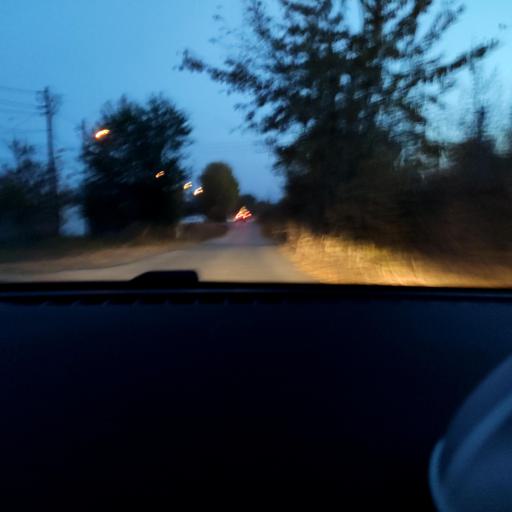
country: RU
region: Samara
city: Petra-Dubrava
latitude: 53.2983
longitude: 50.3038
